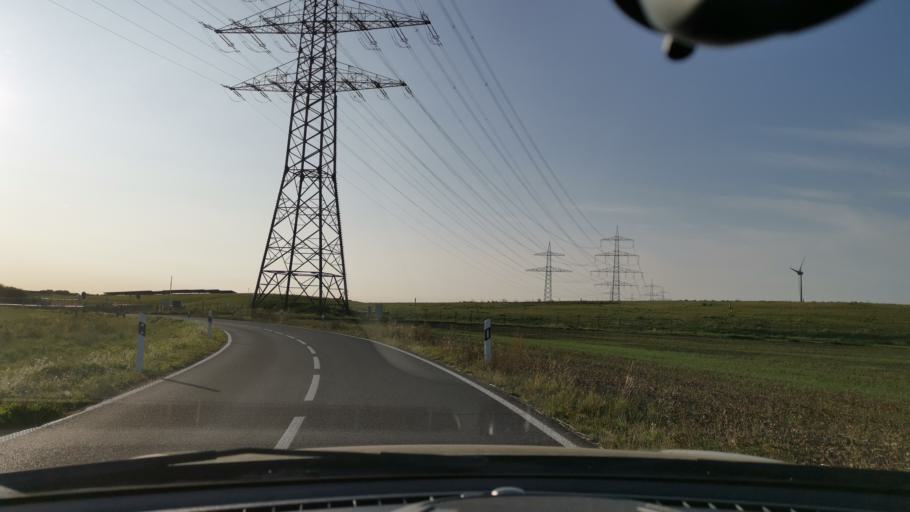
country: DE
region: North Rhine-Westphalia
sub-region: Regierungsbezirk Dusseldorf
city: Rommerskirchen
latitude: 51.0859
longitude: 6.7113
